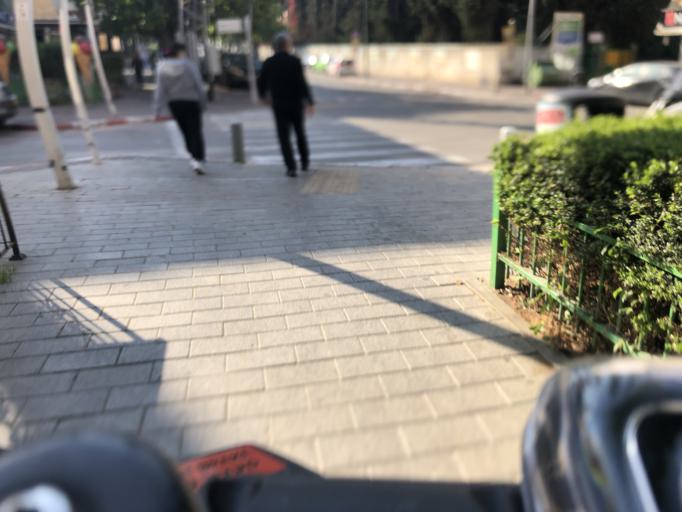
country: IL
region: Tel Aviv
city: Giv`atayim
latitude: 32.0732
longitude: 34.8087
